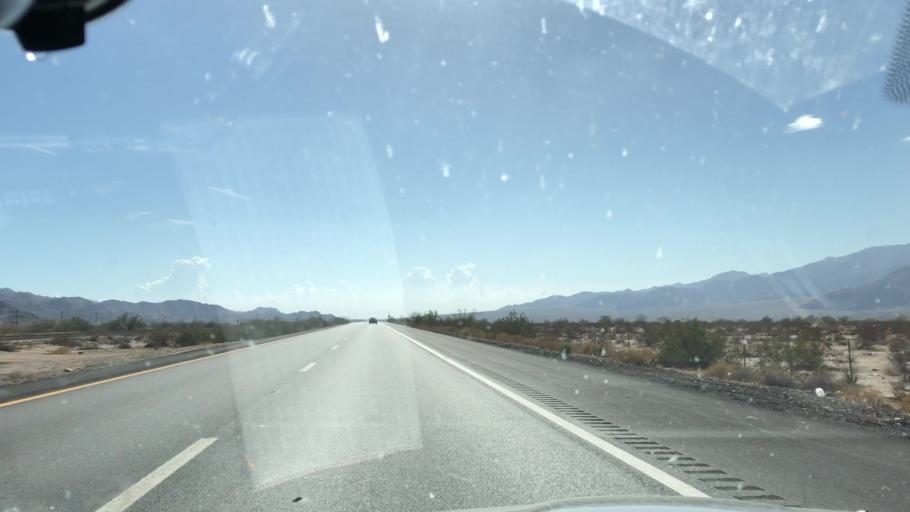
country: US
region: California
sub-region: Imperial County
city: Niland
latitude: 33.6724
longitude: -115.6006
